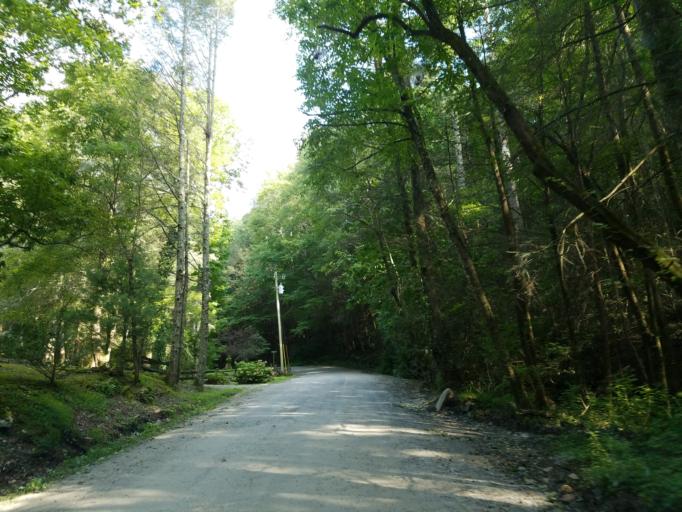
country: US
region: Georgia
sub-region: Fannin County
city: Blue Ridge
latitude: 34.7826
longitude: -84.3384
